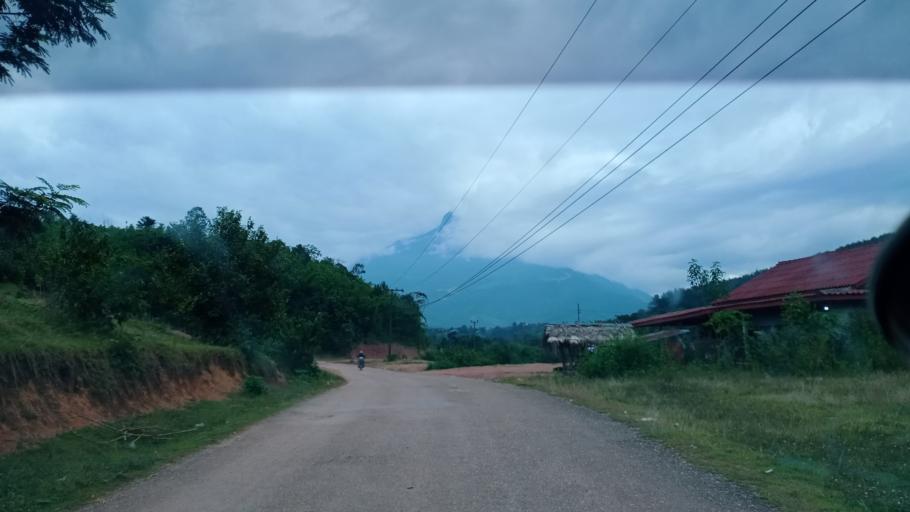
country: TH
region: Changwat Bueng Kan
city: Pak Khat
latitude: 18.6842
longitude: 103.1715
